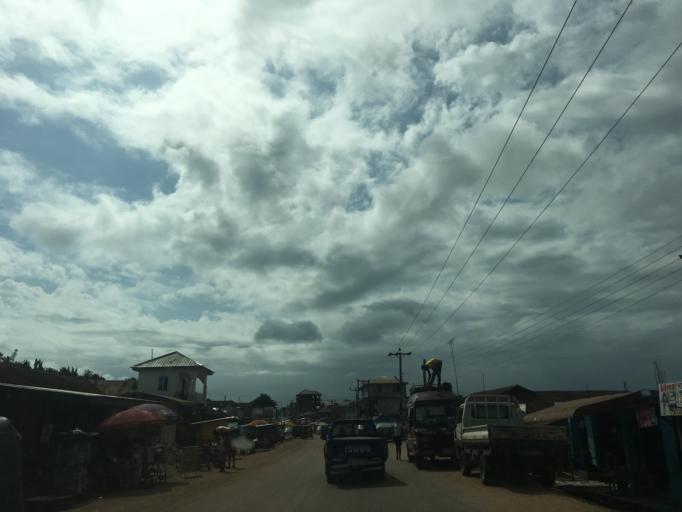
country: GH
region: Western
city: Wassa-Akropong
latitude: 5.8063
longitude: -2.4332
